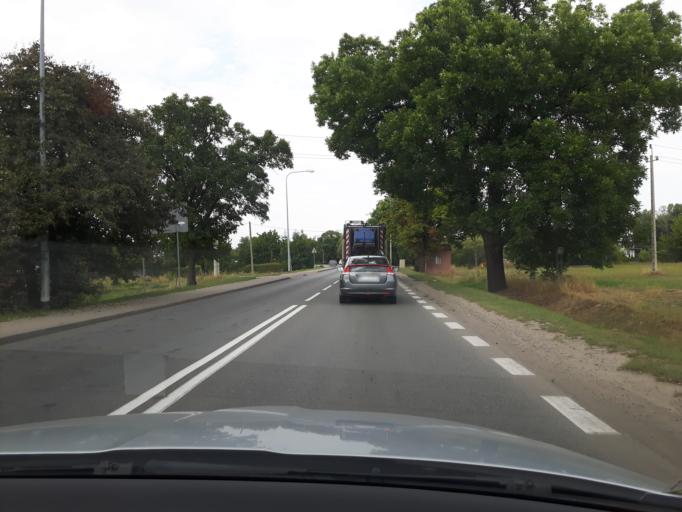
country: PL
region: Masovian Voivodeship
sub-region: Powiat legionowski
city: Stanislawow Pierwszy
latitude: 52.3569
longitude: 21.0288
